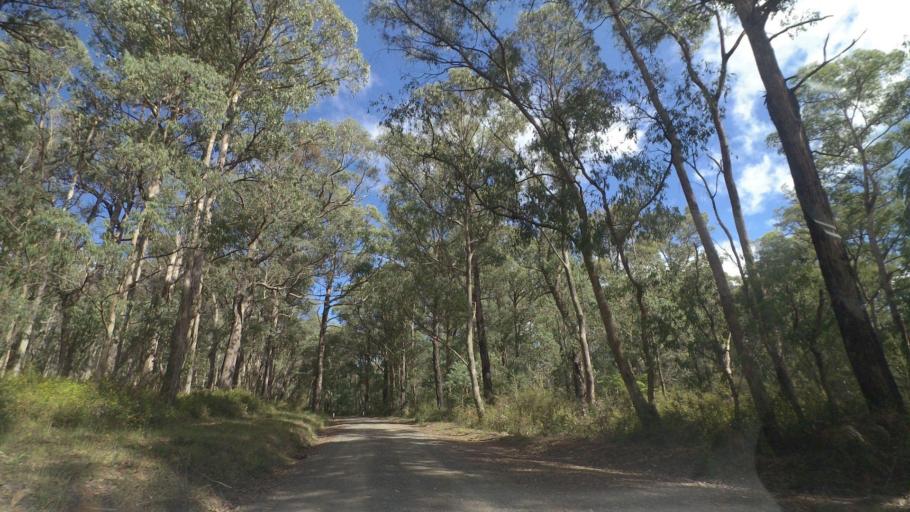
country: AU
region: Victoria
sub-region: Cardinia
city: Gembrook
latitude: -37.9038
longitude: 145.6141
